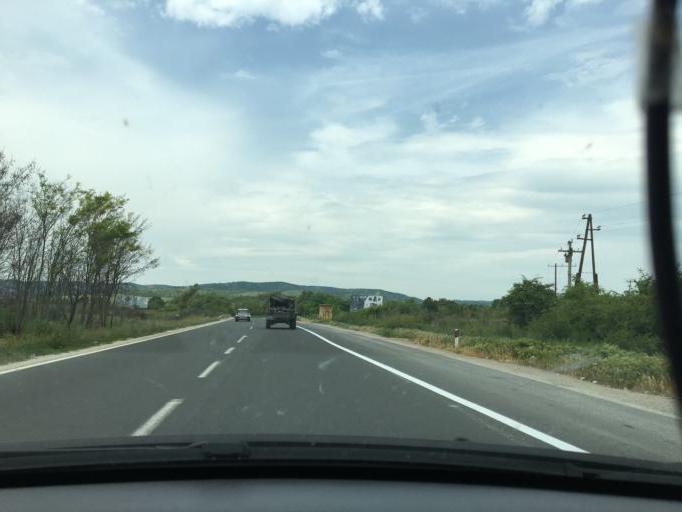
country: MK
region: Veles
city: Veles
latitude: 41.7795
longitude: 21.7665
